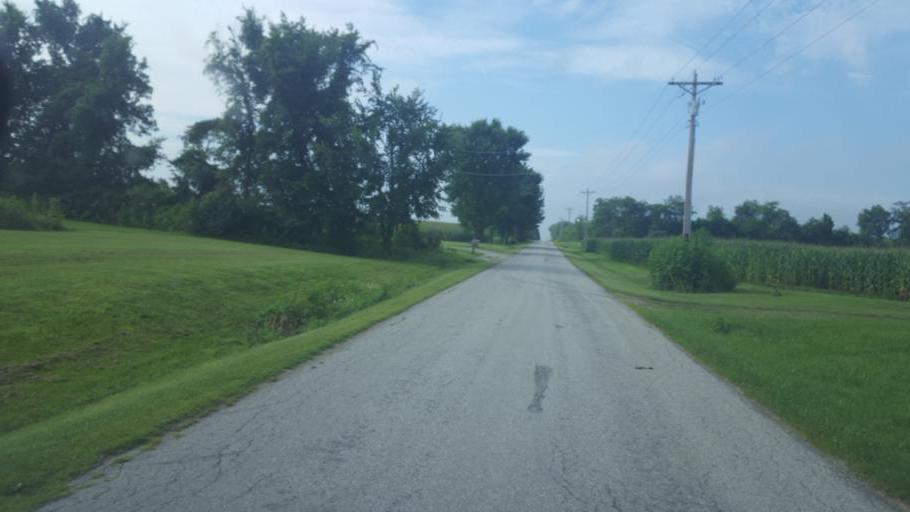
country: US
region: Ohio
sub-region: Delaware County
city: Ashley
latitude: 40.3983
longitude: -82.9112
